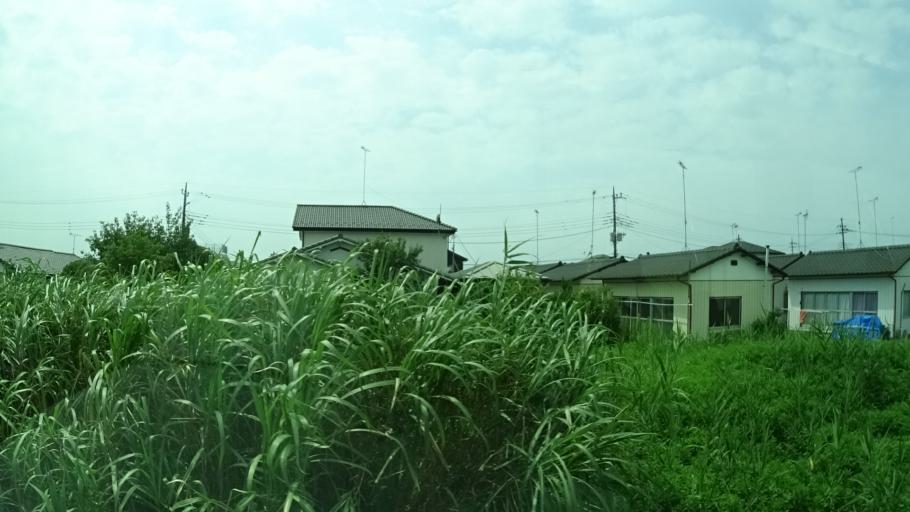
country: JP
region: Tochigi
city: Mashiko
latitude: 36.4641
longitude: 140.0892
